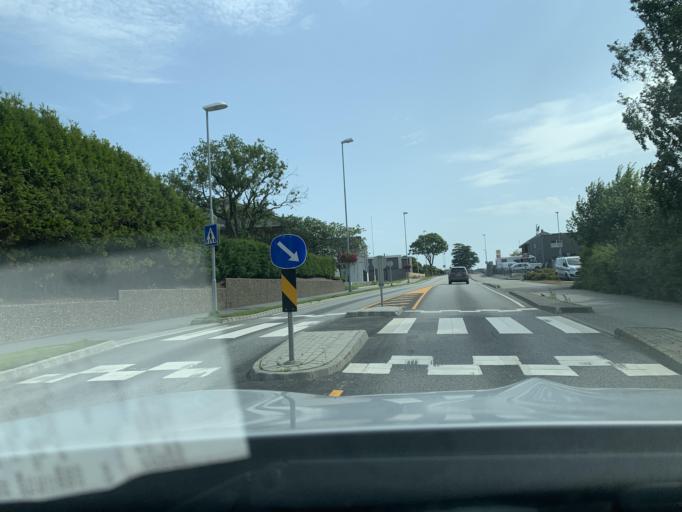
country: NO
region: Rogaland
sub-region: Klepp
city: Kleppe
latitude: 58.7723
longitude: 5.6299
